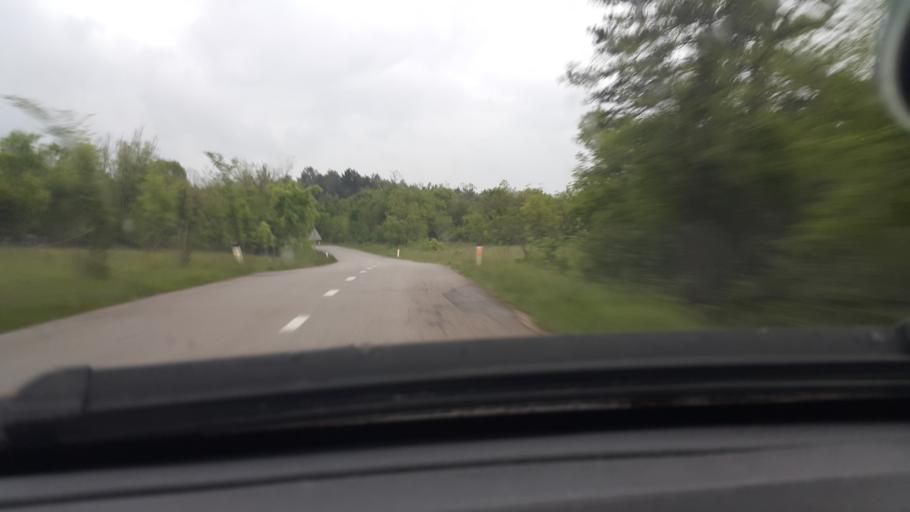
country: SI
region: Sezana
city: Sezana
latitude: 45.7753
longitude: 13.8714
